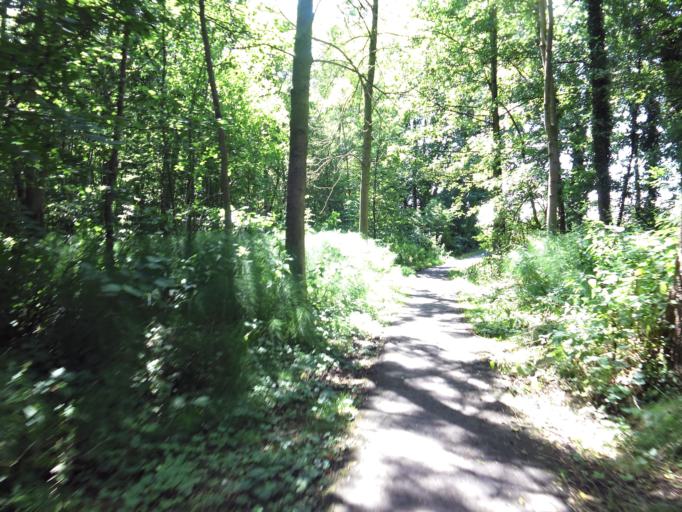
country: NL
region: Limburg
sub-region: Gemeente Voerendaal
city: Voerendaal
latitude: 50.8863
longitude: 5.9331
